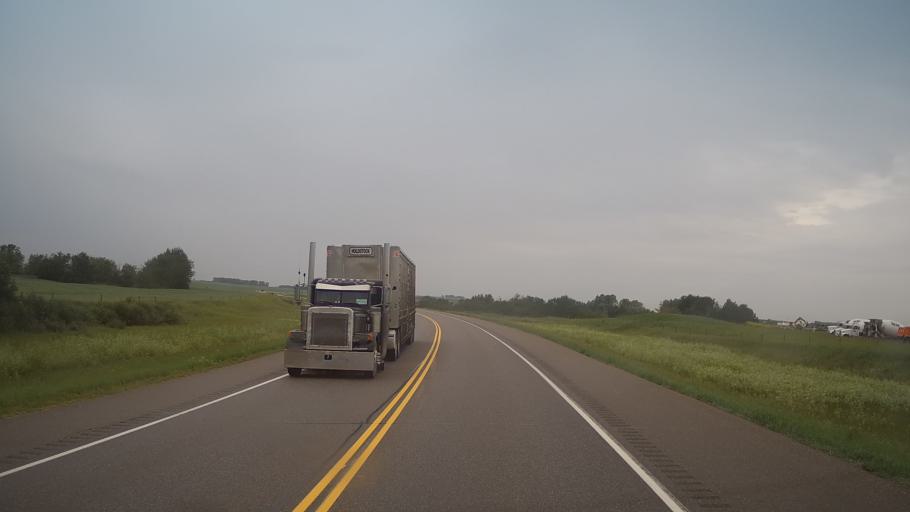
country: CA
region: Saskatchewan
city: Dalmeny
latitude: 52.1289
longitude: -106.8993
